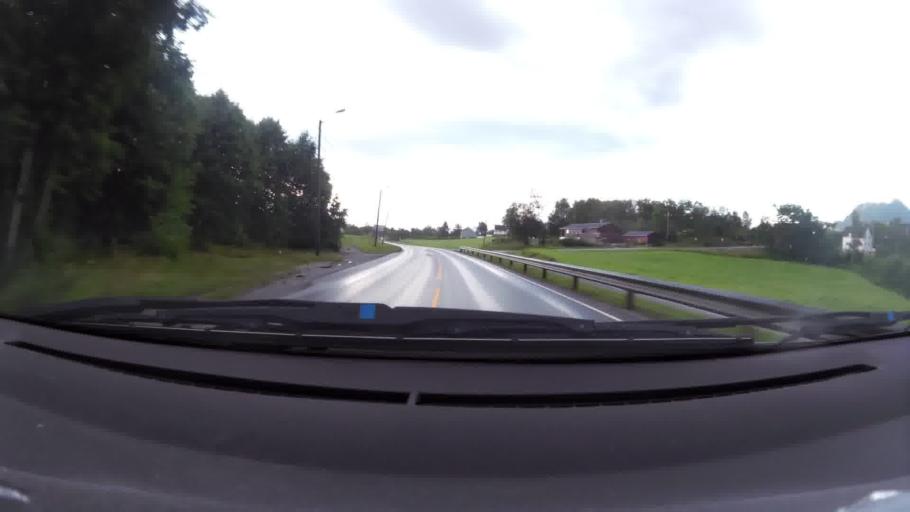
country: NO
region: More og Romsdal
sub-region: Eide
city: Eide
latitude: 62.8953
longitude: 7.4058
